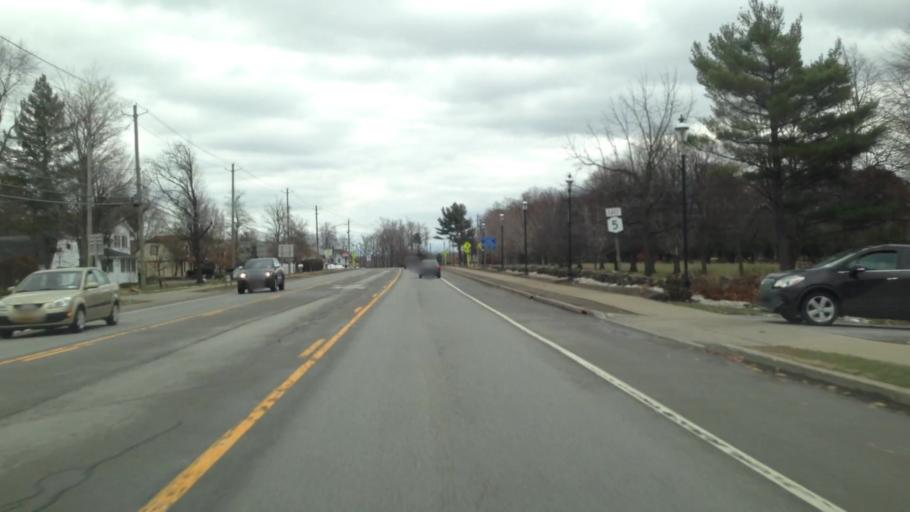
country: US
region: New York
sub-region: Erie County
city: Clarence
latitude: 42.9794
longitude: -78.6017
